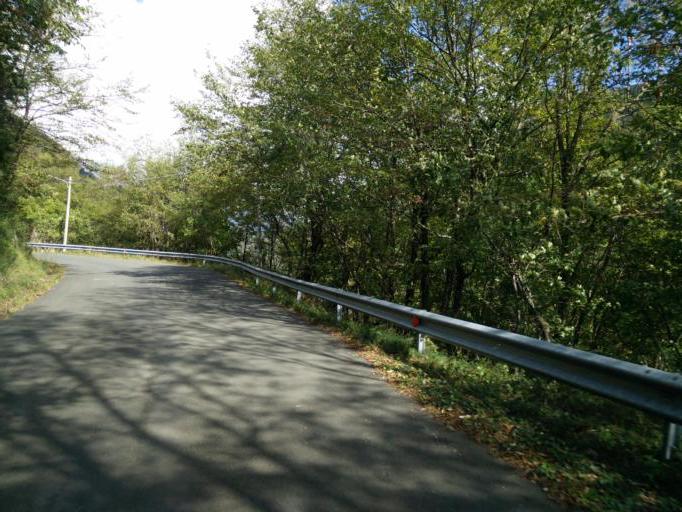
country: IT
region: Liguria
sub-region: Provincia di La Spezia
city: Sesta Godano
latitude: 44.3399
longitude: 9.7035
